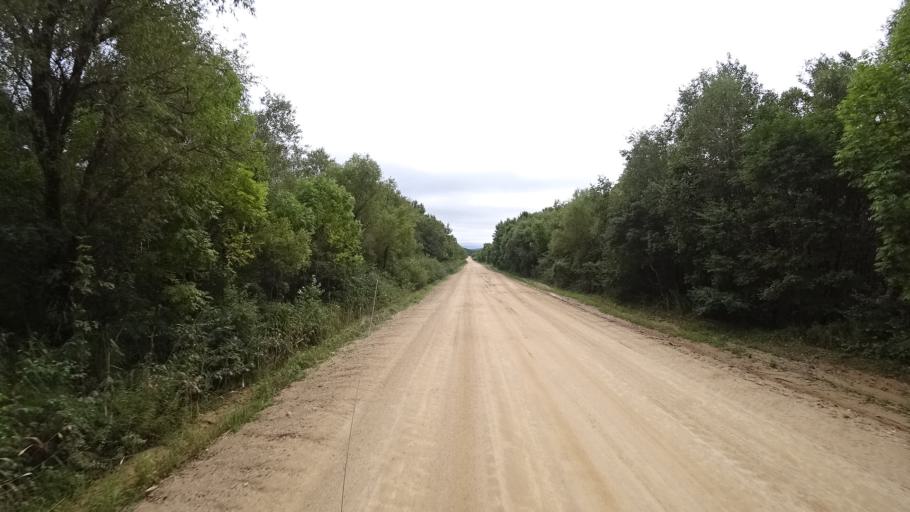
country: RU
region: Primorskiy
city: Monastyrishche
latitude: 44.1079
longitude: 132.6158
